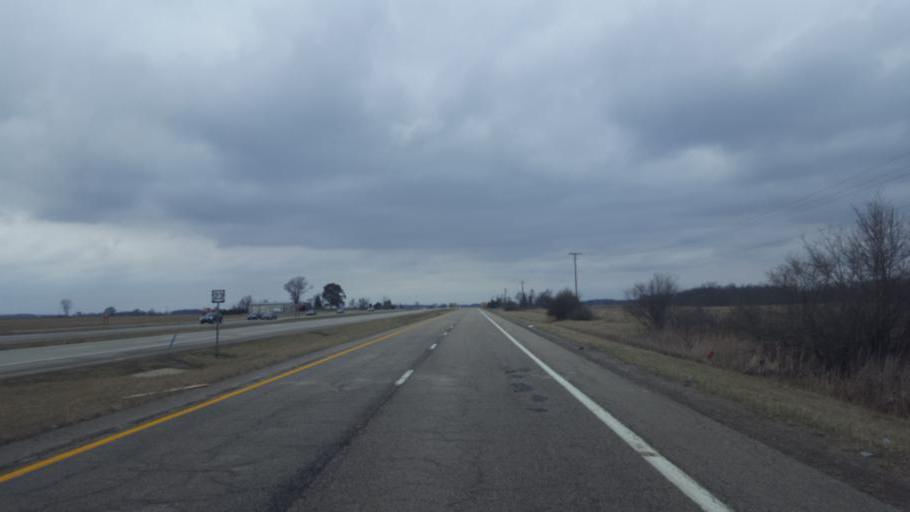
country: US
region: Ohio
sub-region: Delaware County
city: Delaware
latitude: 40.3895
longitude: -83.0735
